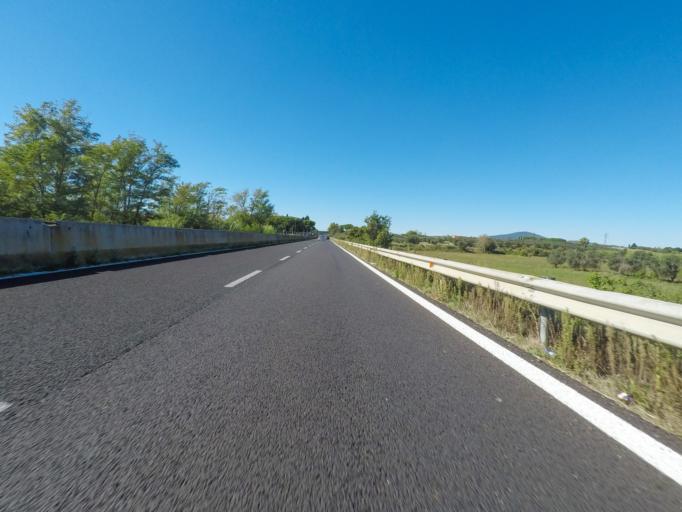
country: IT
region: Latium
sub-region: Provincia di Viterbo
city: Pescia Romana
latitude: 42.4010
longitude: 11.5045
